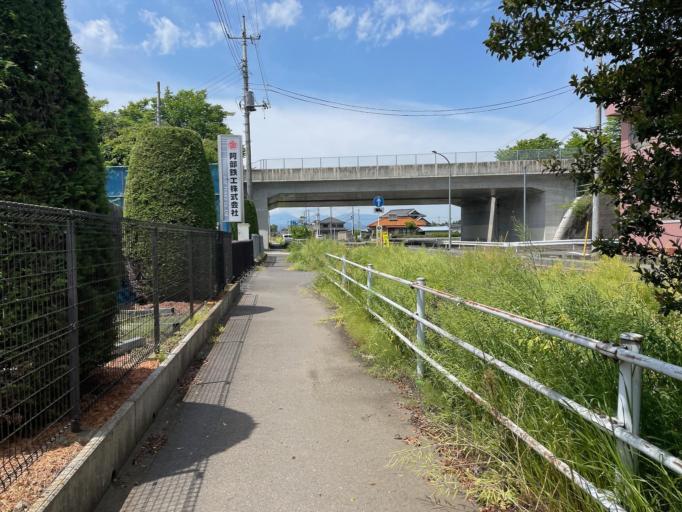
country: JP
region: Tochigi
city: Mibu
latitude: 36.4437
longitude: 139.7836
